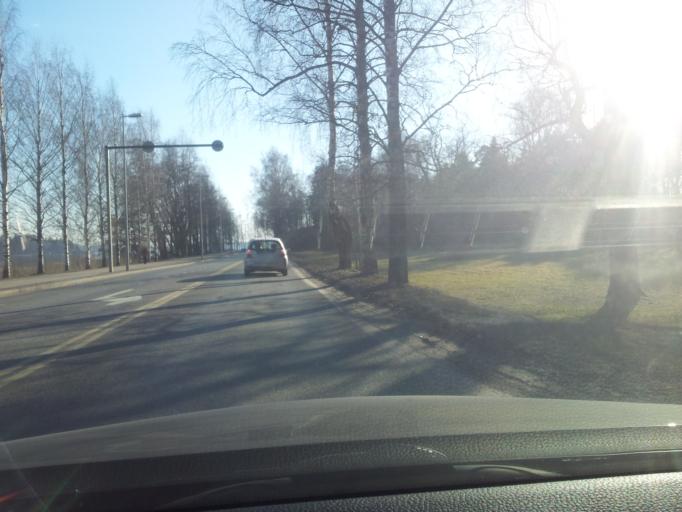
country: FI
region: Uusimaa
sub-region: Helsinki
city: Teekkarikylae
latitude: 60.1916
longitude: 24.8777
